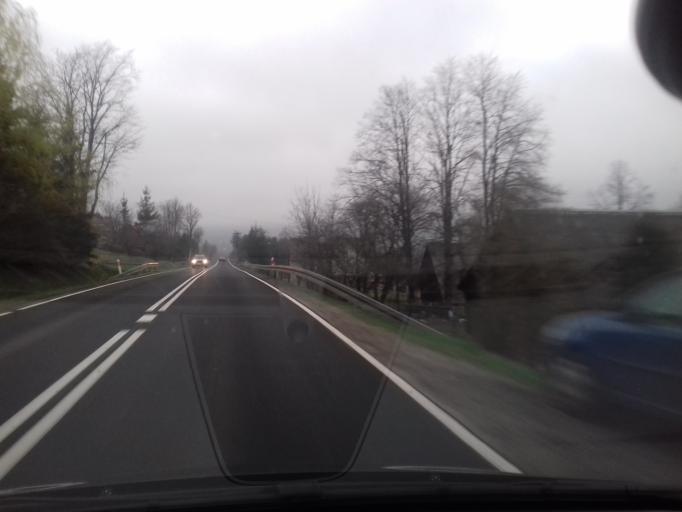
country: PL
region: Lesser Poland Voivodeship
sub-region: Powiat limanowski
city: Dobra
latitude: 49.7108
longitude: 20.2487
